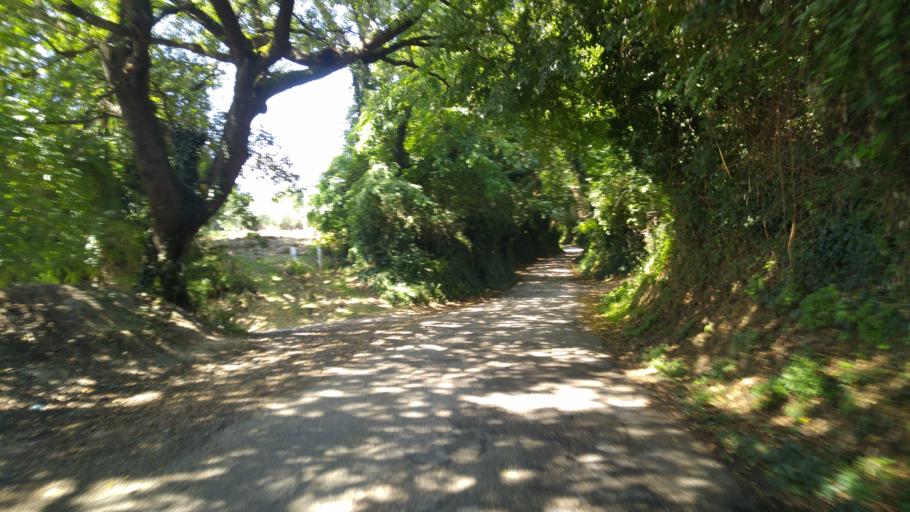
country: IT
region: The Marches
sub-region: Provincia di Pesaro e Urbino
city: Centinarola
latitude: 43.8157
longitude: 12.9762
